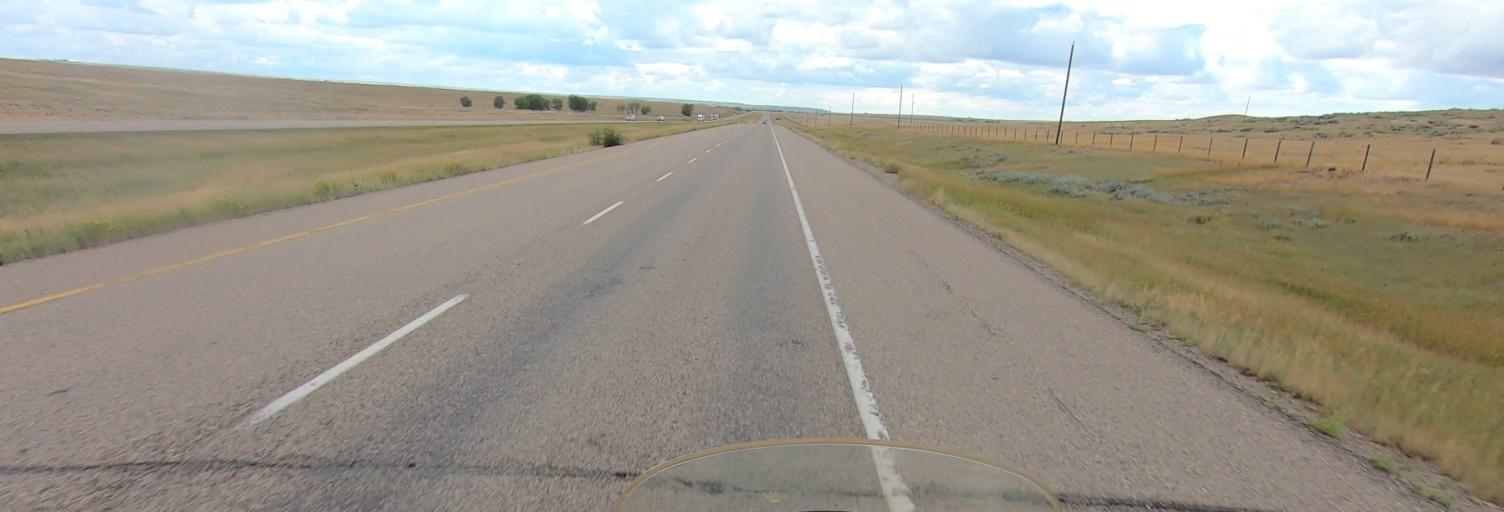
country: CA
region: Alberta
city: Medicine Hat
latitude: 49.9402
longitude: -110.0918
